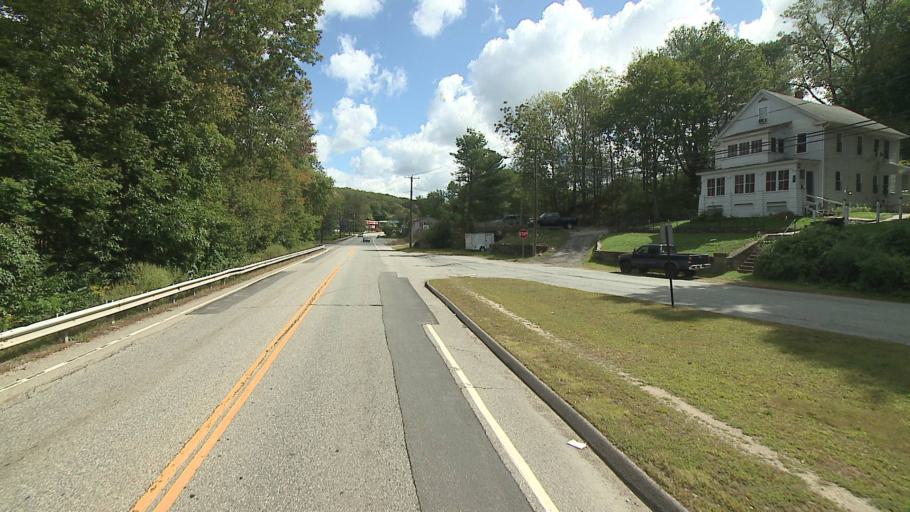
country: US
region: Connecticut
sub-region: Windham County
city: Putnam
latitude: 41.9240
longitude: -71.8961
